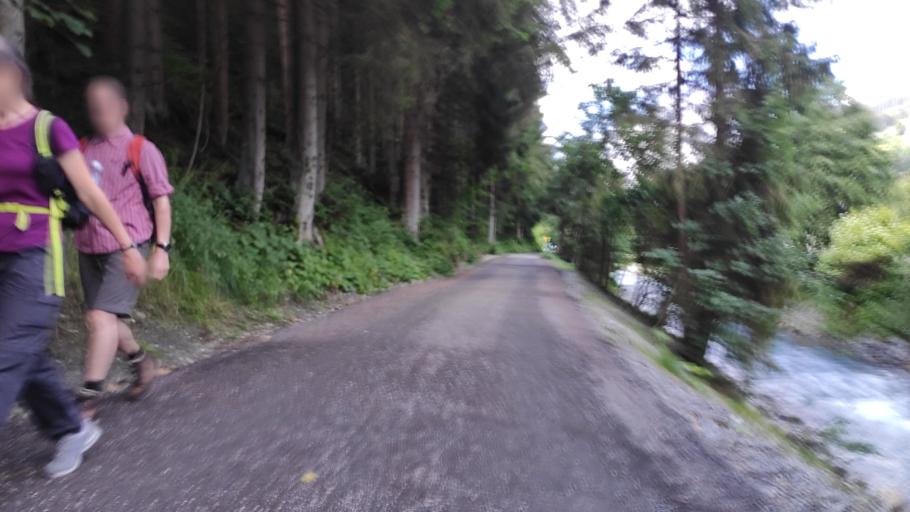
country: AT
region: Salzburg
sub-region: Politischer Bezirk Zell am See
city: Saalbach
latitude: 47.3890
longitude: 12.6248
